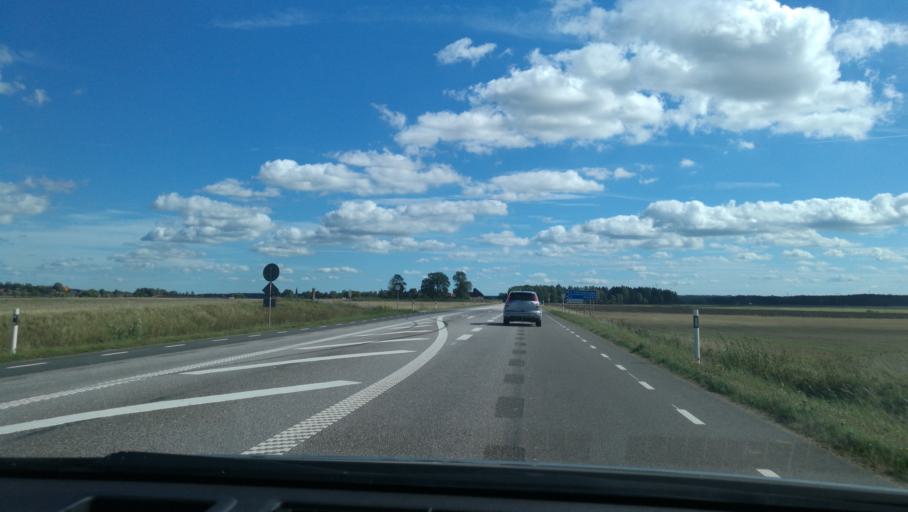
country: SE
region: Vaestra Goetaland
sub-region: Gotene Kommun
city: Kallby
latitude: 58.5099
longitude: 13.3740
